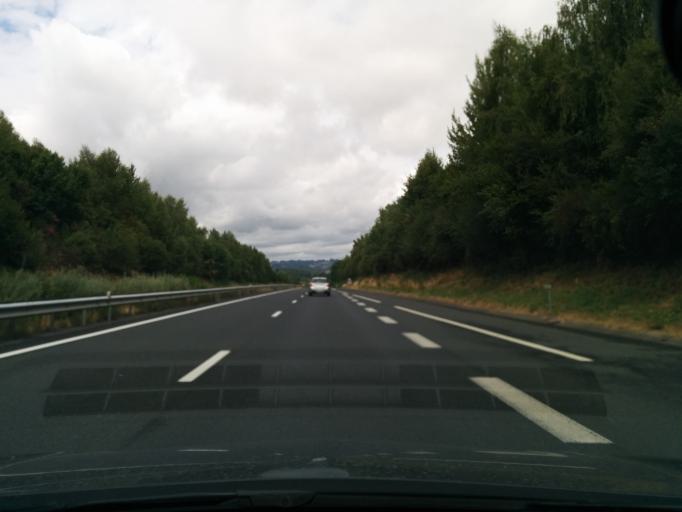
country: FR
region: Limousin
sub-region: Departement de la Correze
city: Uzerche
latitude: 45.3974
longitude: 1.5665
